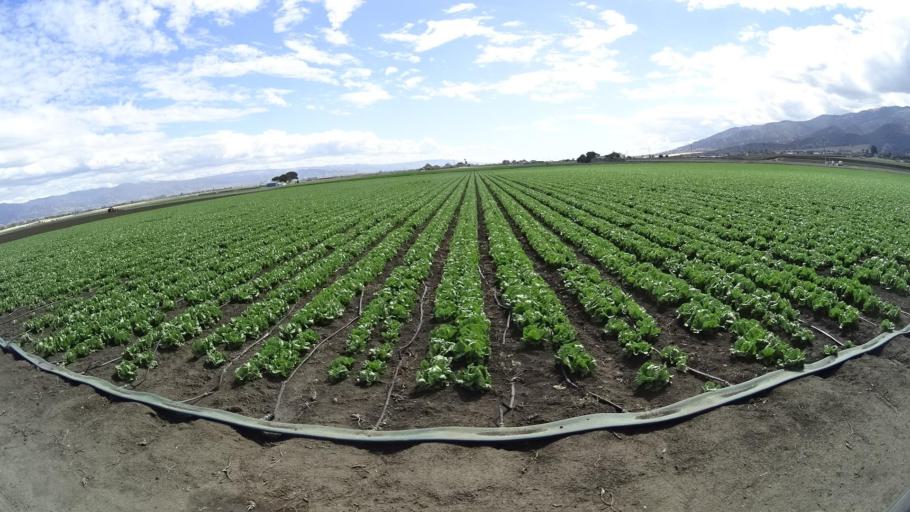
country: US
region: California
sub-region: Monterey County
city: Salinas
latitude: 36.6015
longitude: -121.6069
